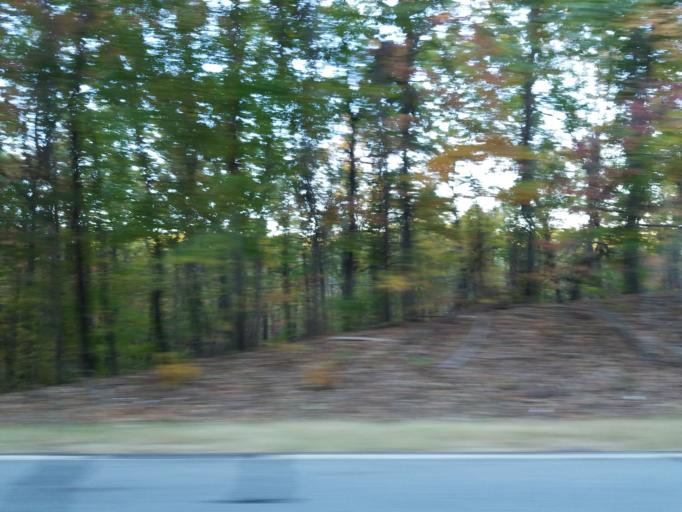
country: US
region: Georgia
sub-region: Lumpkin County
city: Dahlonega
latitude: 34.5357
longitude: -84.0712
